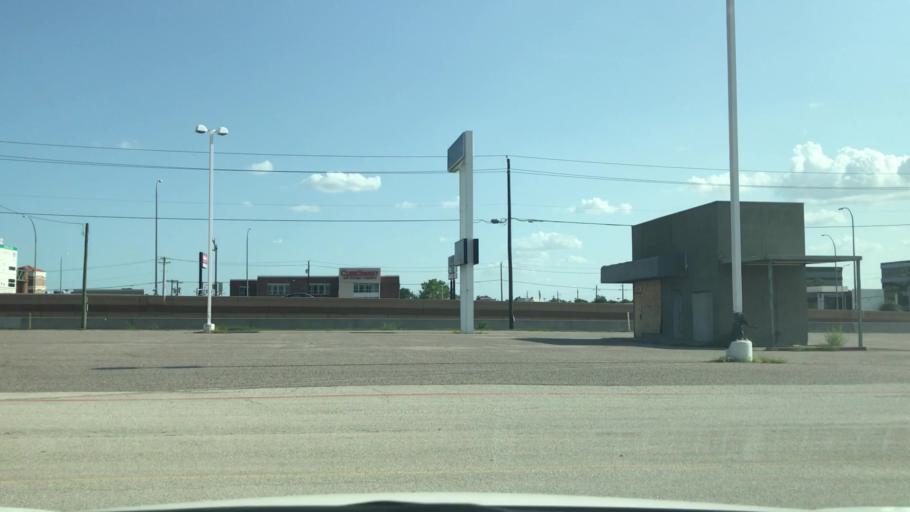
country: US
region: Texas
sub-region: Dallas County
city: Addison
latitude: 32.9271
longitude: -96.8069
